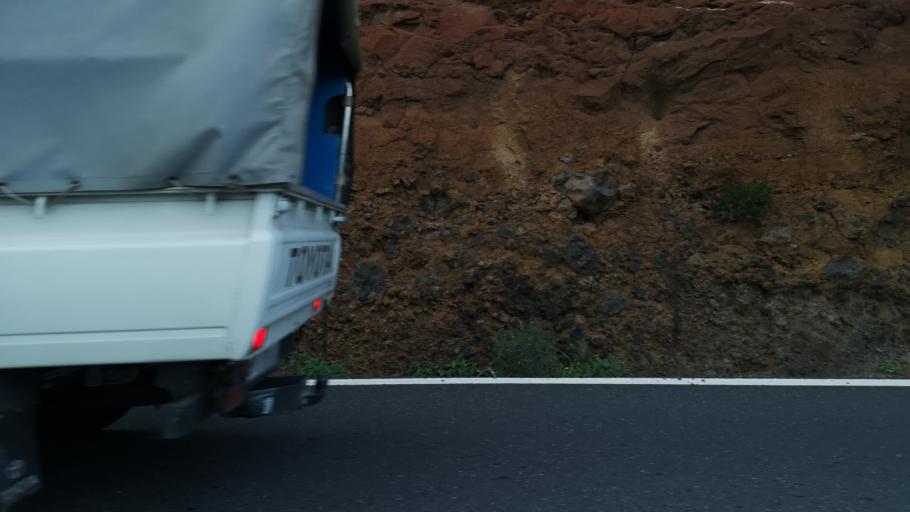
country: ES
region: Canary Islands
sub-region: Provincia de Santa Cruz de Tenerife
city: San Sebastian de la Gomera
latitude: 28.0809
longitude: -17.1286
